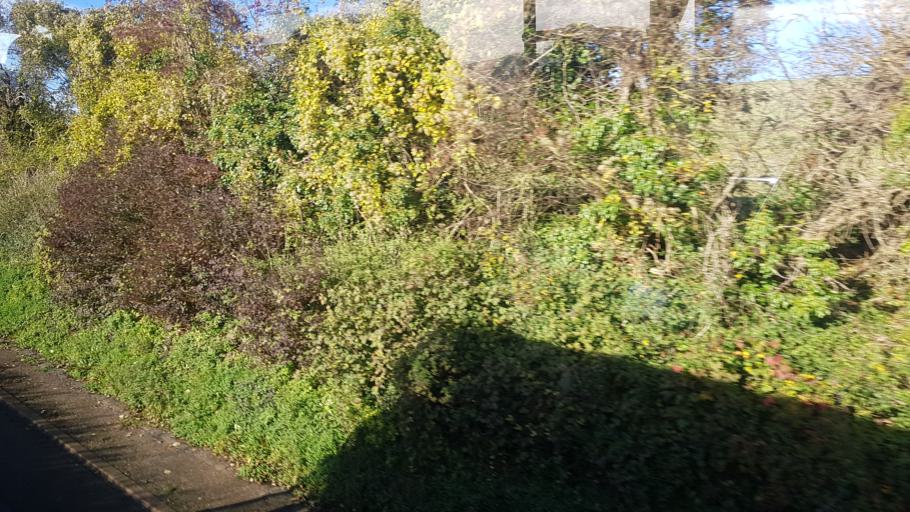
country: GB
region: England
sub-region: Isle of Wight
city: Newport
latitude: 50.6823
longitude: -1.3327
